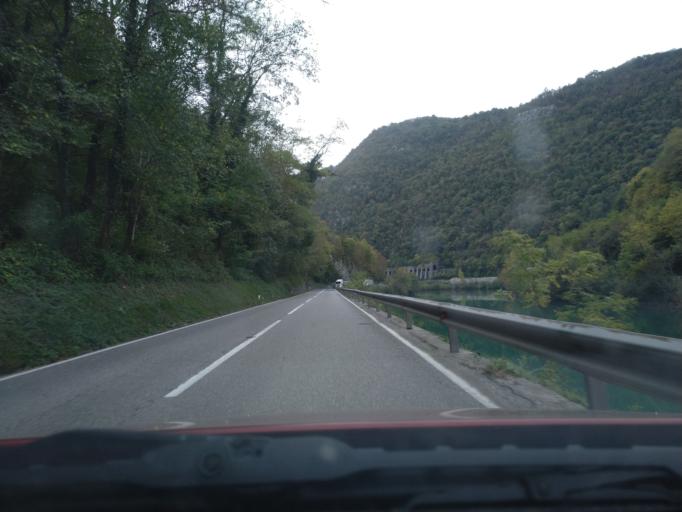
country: SI
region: Kanal
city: Deskle
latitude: 46.0217
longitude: 13.6072
